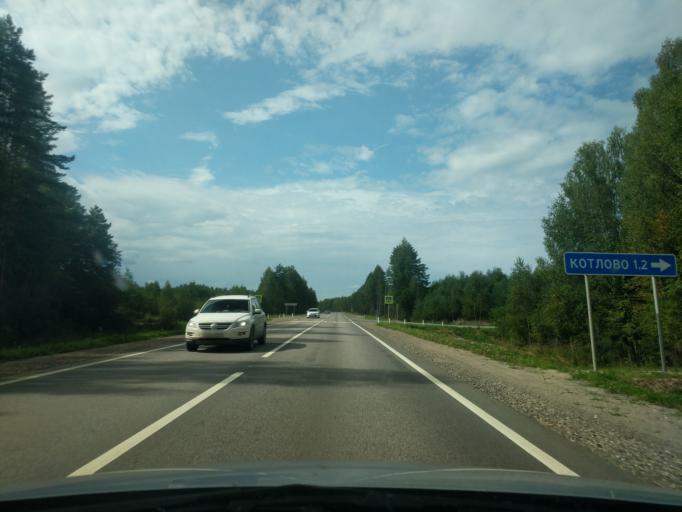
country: RU
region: Kostroma
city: Kadyy
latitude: 57.7977
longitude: 42.8850
